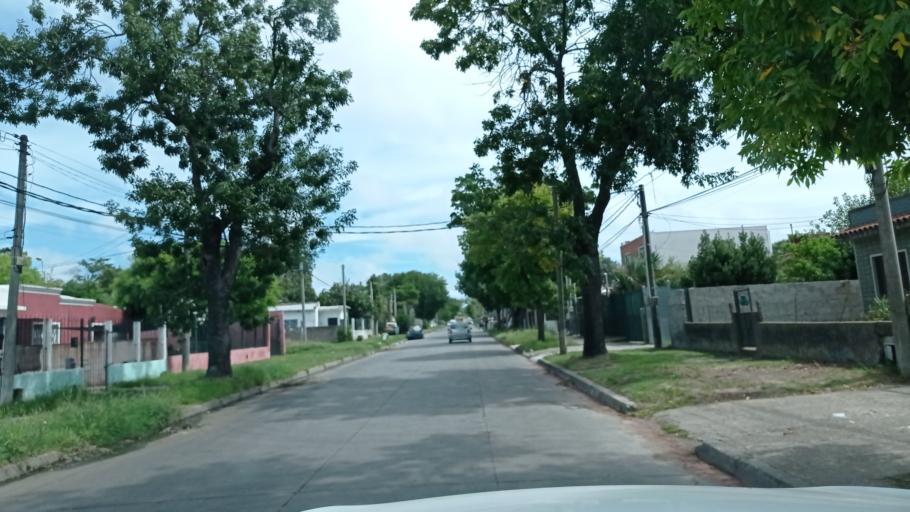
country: UY
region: Canelones
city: Paso de Carrasco
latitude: -34.8658
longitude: -56.1238
